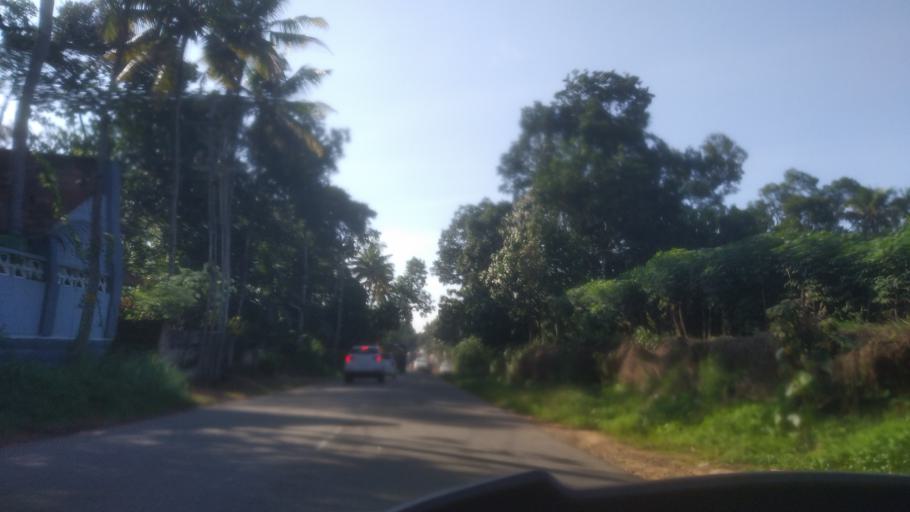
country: IN
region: Kerala
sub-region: Ernakulam
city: Muvattupuzha
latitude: 9.9766
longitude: 76.5287
